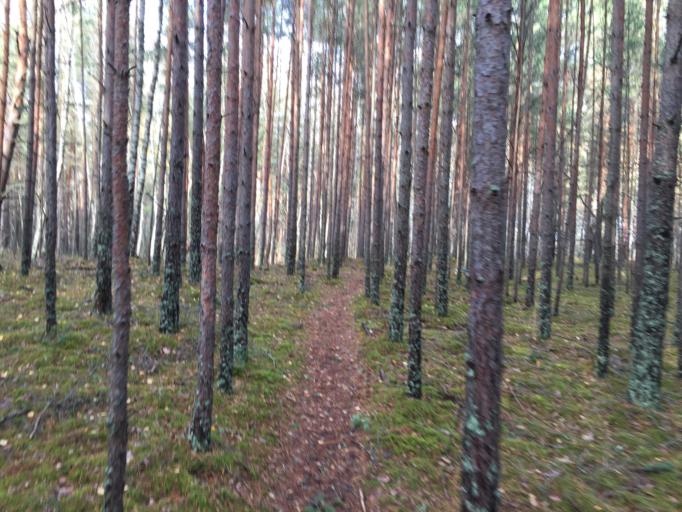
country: LV
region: Carnikava
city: Carnikava
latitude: 57.1506
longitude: 24.2590
